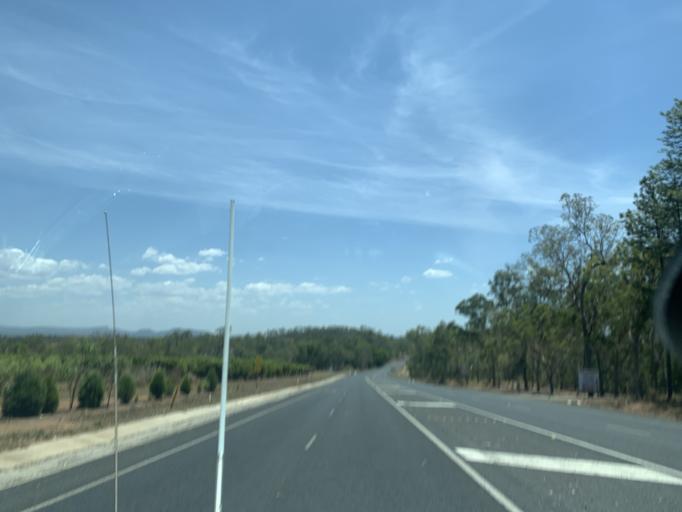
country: AU
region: Queensland
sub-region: Tablelands
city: Mareeba
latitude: -16.9875
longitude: 145.5185
